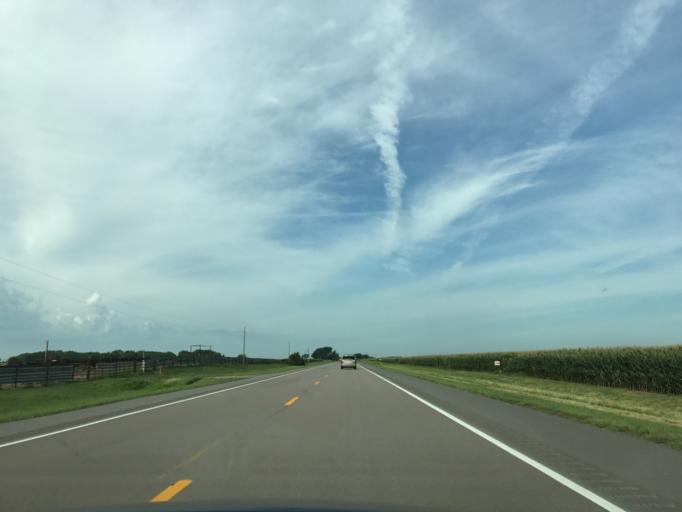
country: US
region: Nebraska
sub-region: Saline County
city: Friend
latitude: 40.6547
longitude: -97.1427
